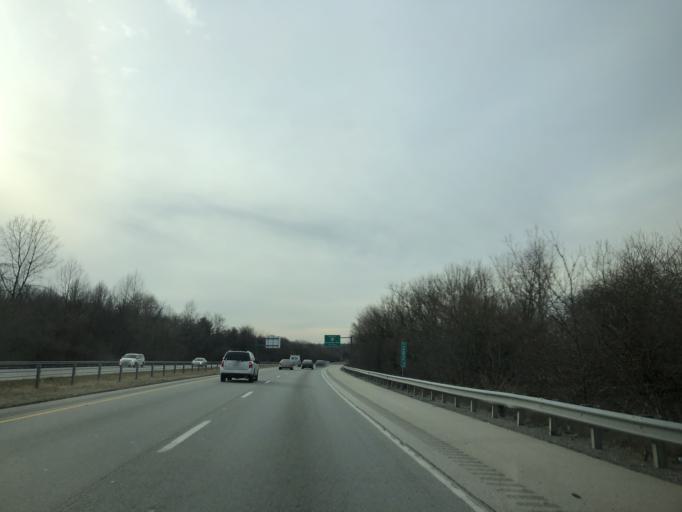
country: US
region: Pennsylvania
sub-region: Chester County
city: Exton
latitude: 40.0135
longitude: -75.6452
